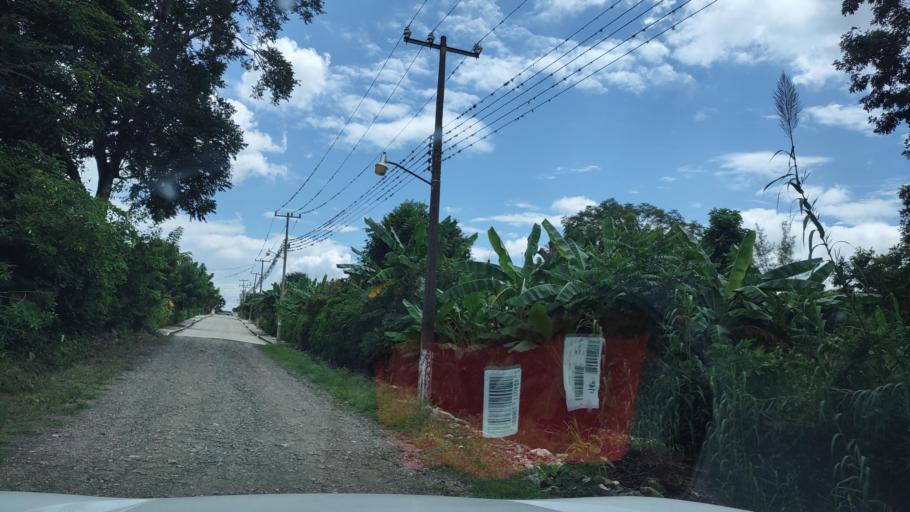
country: MX
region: Veracruz
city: Cerro Azul
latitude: 21.2441
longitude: -97.8011
